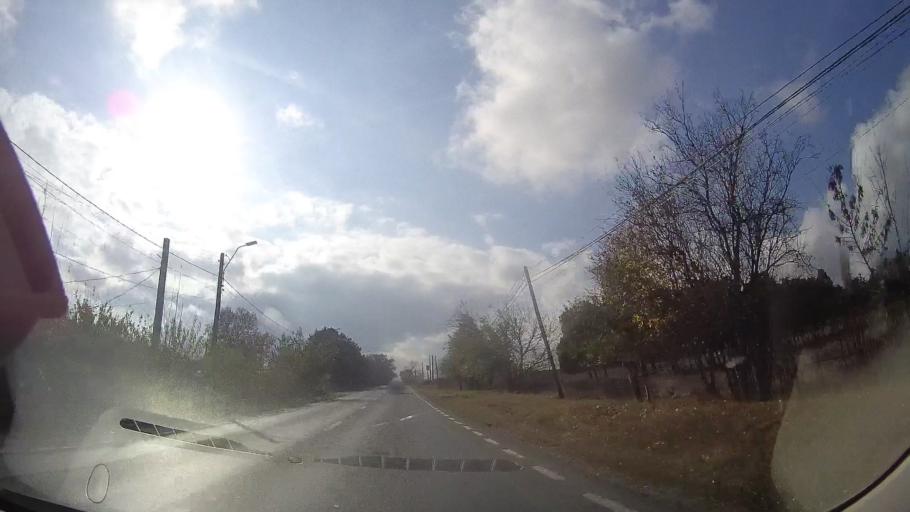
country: RO
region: Constanta
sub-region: Comuna Agigea
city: Agigea
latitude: 44.0866
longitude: 28.6085
